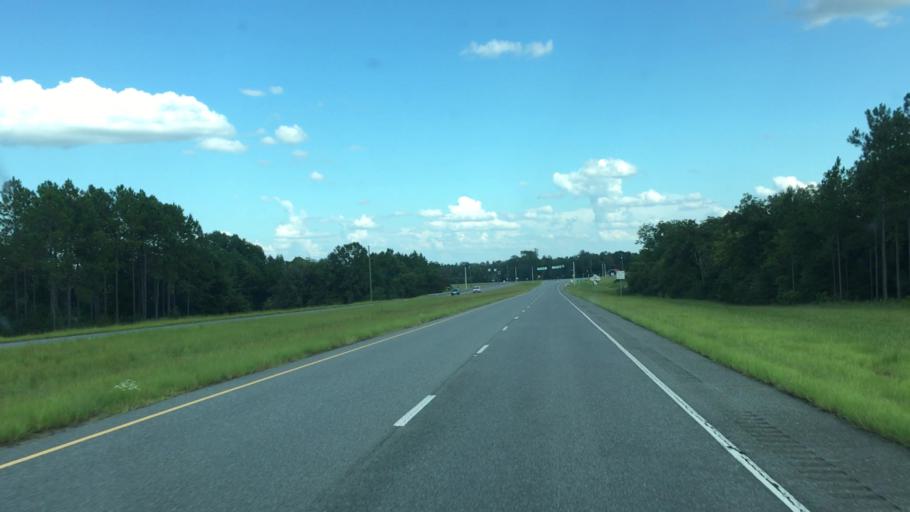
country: US
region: Georgia
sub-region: Laurens County
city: Dublin
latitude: 32.5009
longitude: -82.9345
